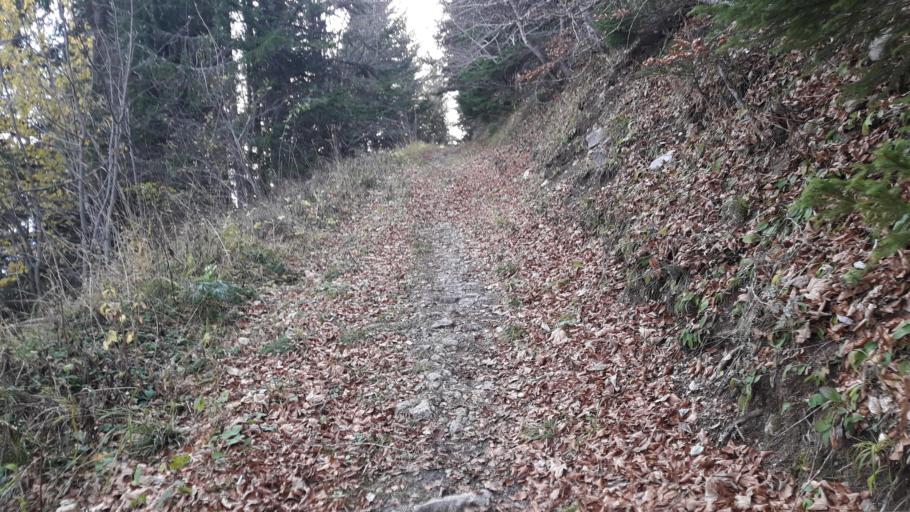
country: FR
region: Rhone-Alpes
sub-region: Departement de l'Isere
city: Bernin
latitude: 45.2981
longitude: 5.8365
